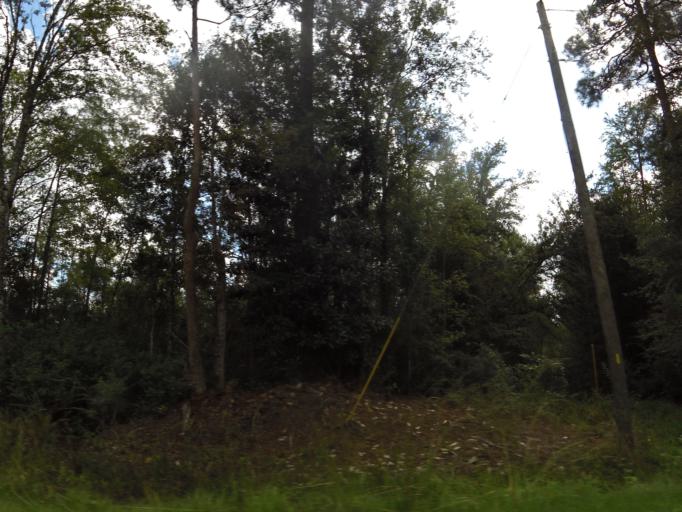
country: US
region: Georgia
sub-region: Brantley County
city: Nahunta
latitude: 31.2060
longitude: -81.9926
